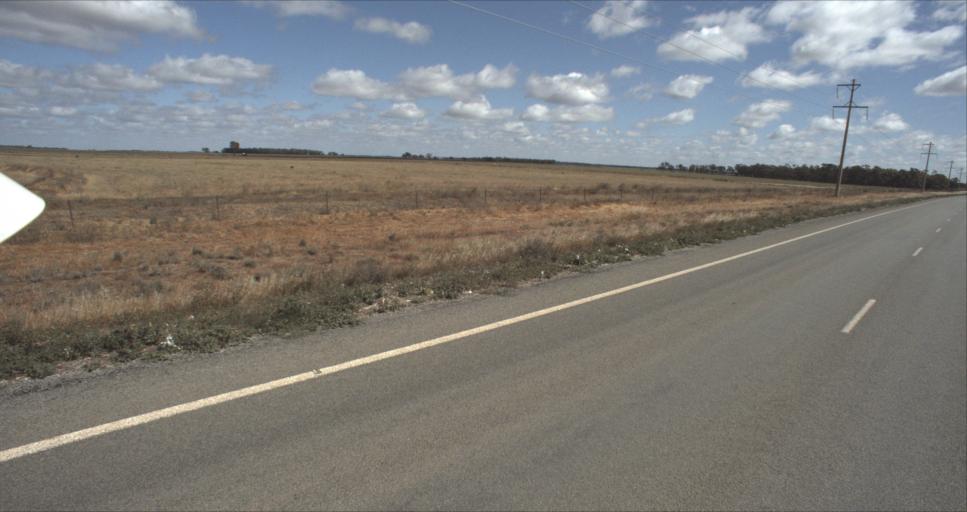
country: AU
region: New South Wales
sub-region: Murrumbidgee Shire
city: Darlington Point
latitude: -34.5815
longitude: 146.1650
